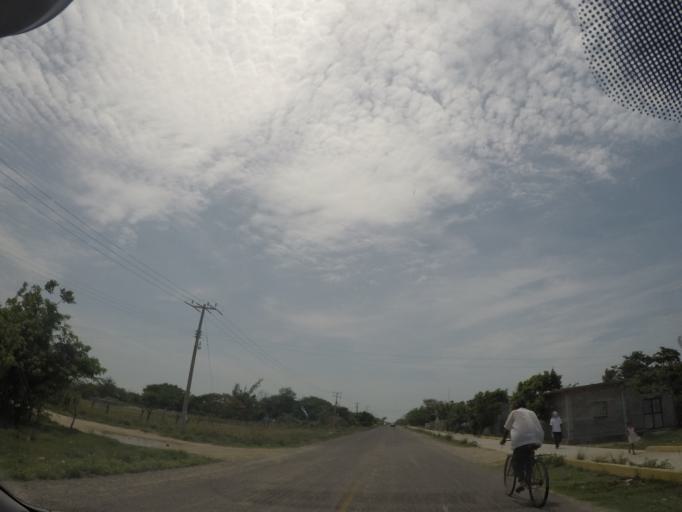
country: MX
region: Oaxaca
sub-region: San Mateo del Mar
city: Colonia Juarez
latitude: 16.2090
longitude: -95.0345
